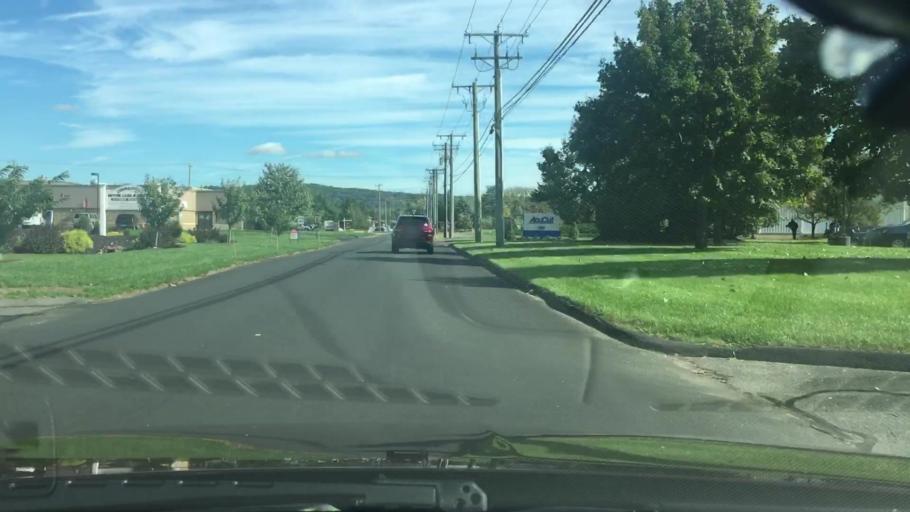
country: US
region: Connecticut
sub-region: Hartford County
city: Plainville
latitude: 41.6500
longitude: -72.8794
